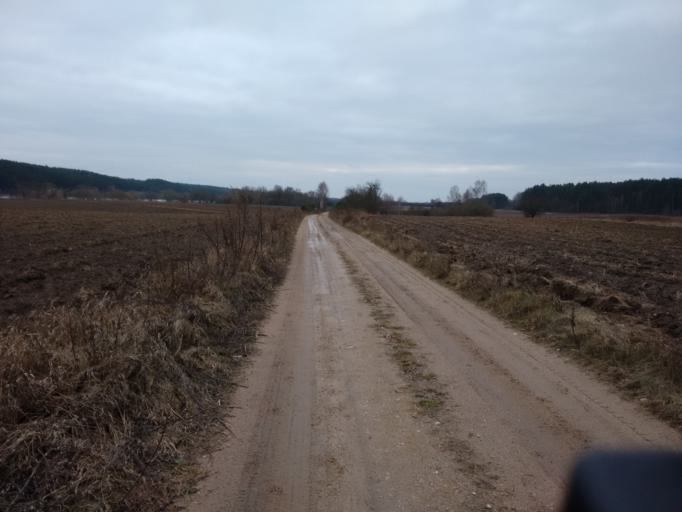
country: LT
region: Alytaus apskritis
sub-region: Alytus
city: Alytus
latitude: 54.2330
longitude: 23.9601
